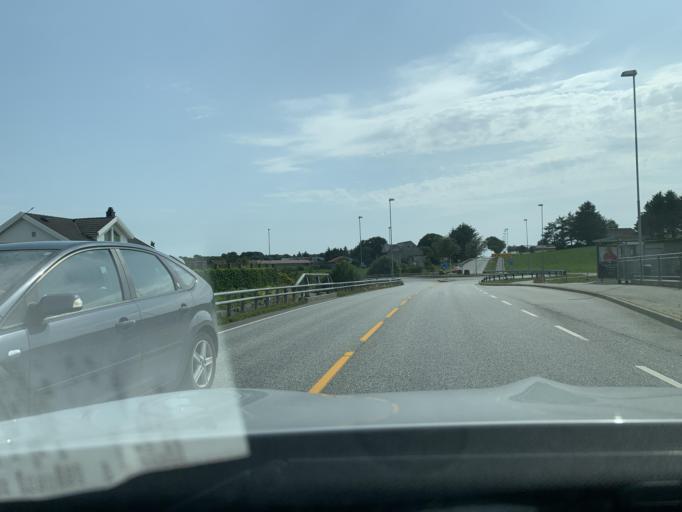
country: NO
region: Rogaland
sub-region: Klepp
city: Kleppe
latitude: 58.7680
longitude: 5.6290
